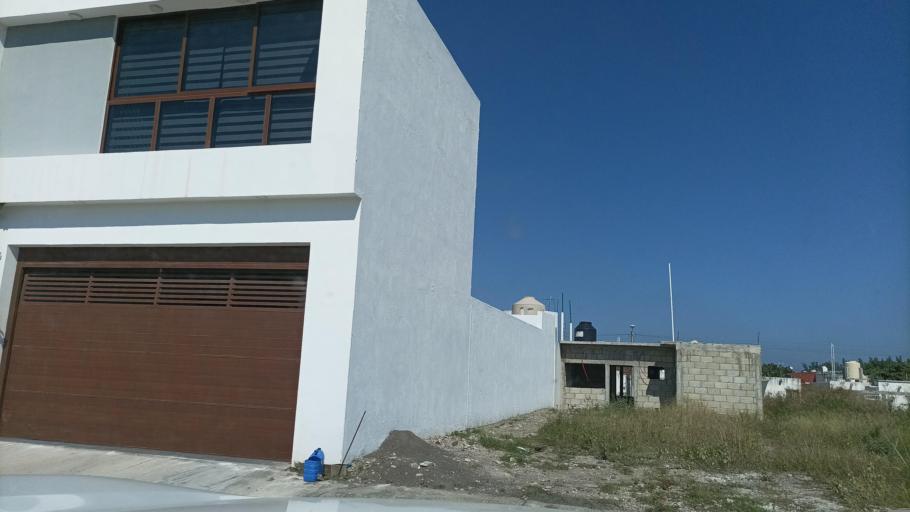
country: MX
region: Veracruz
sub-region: Veracruz
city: Rio Medio [Granja]
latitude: 19.2022
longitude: -96.1799
